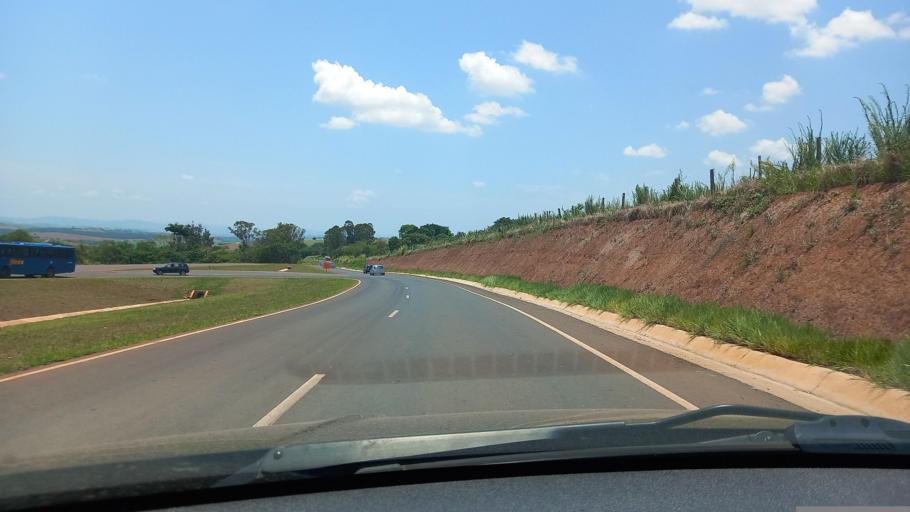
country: BR
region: Sao Paulo
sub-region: Moji-Guacu
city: Mogi-Gaucu
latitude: -22.3391
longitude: -46.8822
